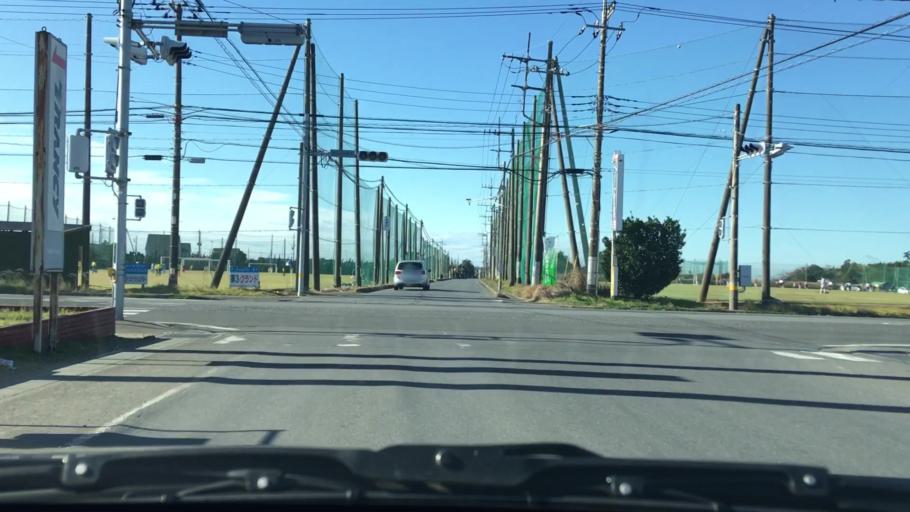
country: JP
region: Chiba
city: Omigawa
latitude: 35.8645
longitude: 140.7111
